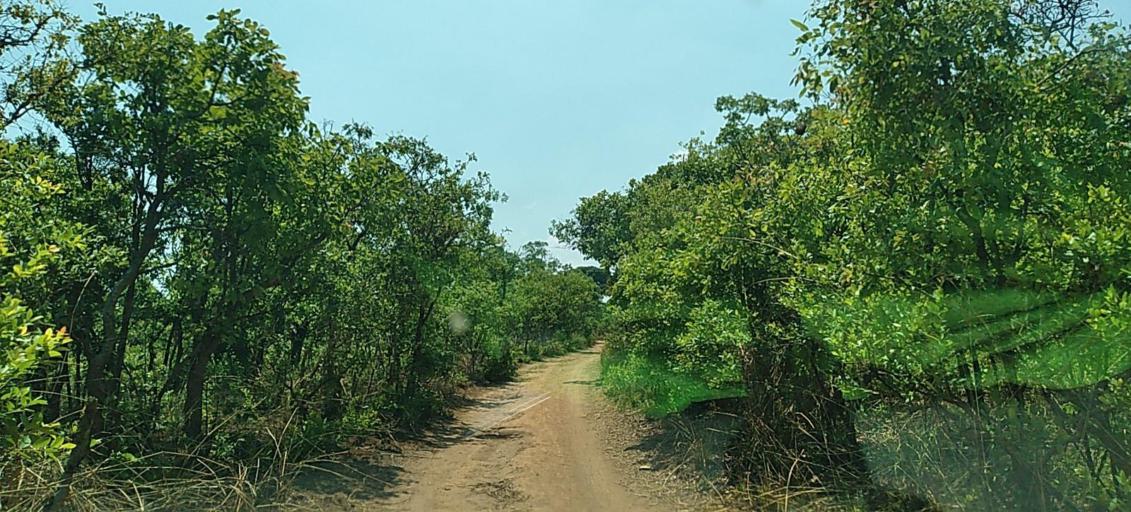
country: CD
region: Katanga
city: Kolwezi
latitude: -11.2887
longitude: 25.2007
